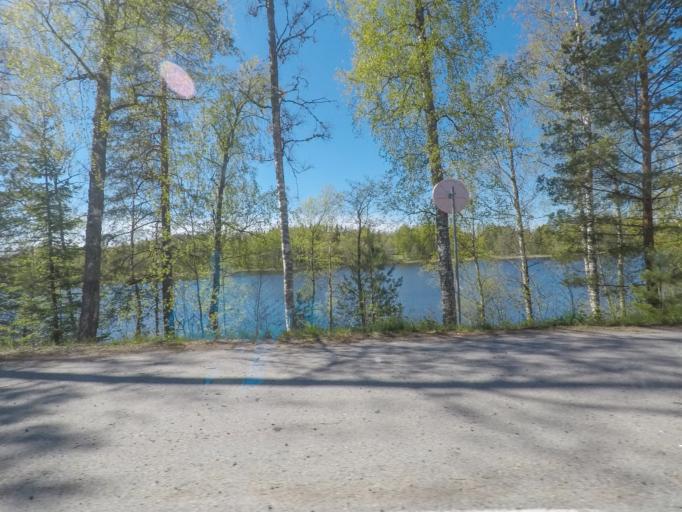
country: FI
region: Uusimaa
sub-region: Helsinki
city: Sammatti
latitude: 60.3408
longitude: 23.8011
